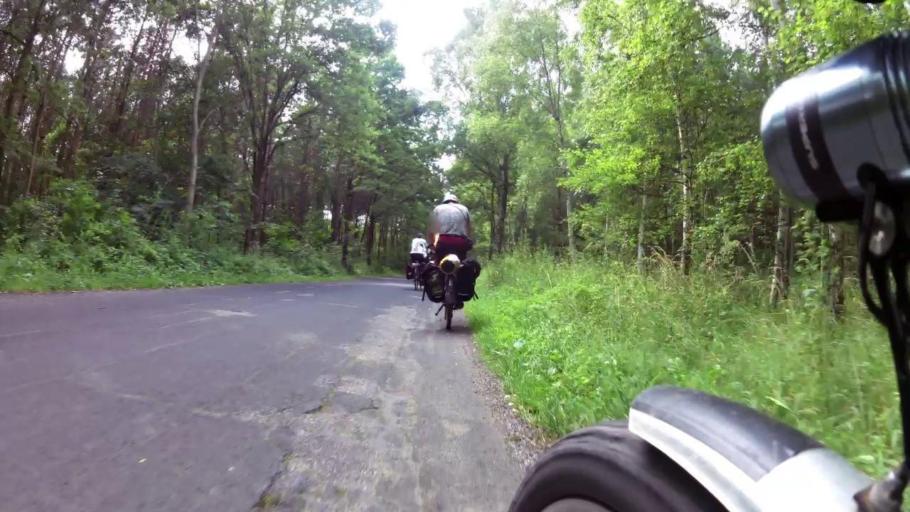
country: PL
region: West Pomeranian Voivodeship
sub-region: Powiat mysliborski
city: Debno
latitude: 52.7878
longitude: 14.6795
